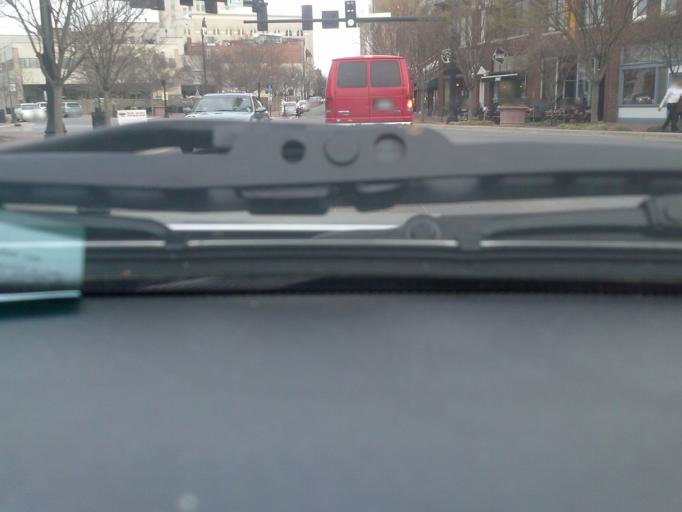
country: US
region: North Carolina
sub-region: Durham County
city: Durham
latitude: 35.9971
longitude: -78.9044
